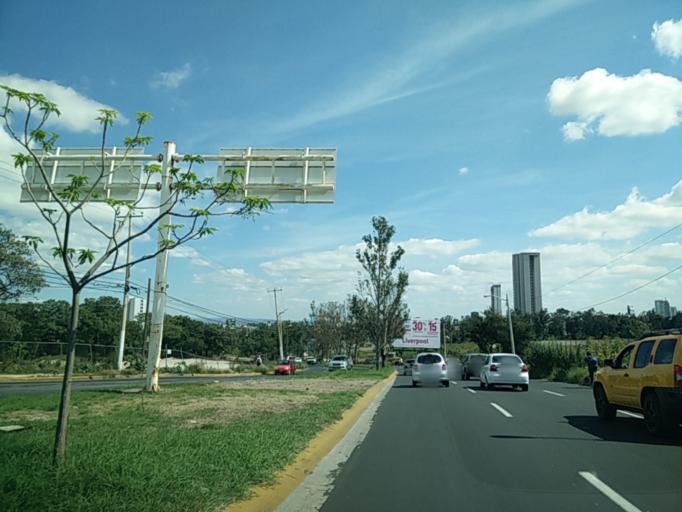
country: MX
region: Jalisco
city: Zapopan2
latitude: 20.7210
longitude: -103.4300
